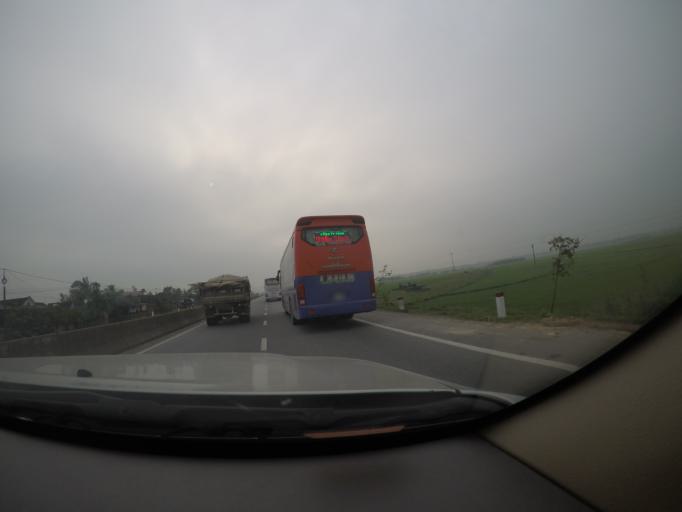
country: VN
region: Ha Tinh
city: Cam Xuyen
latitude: 18.2230
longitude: 106.0676
